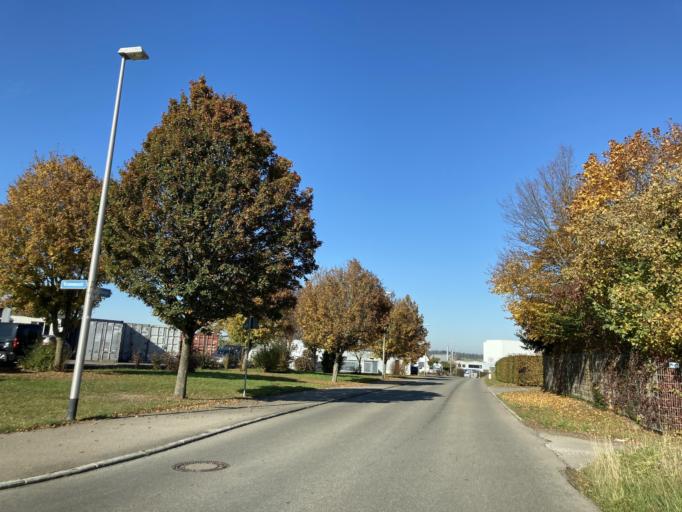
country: DE
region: Baden-Wuerttemberg
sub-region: Tuebingen Region
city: Ofterdingen
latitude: 48.4155
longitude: 9.0396
